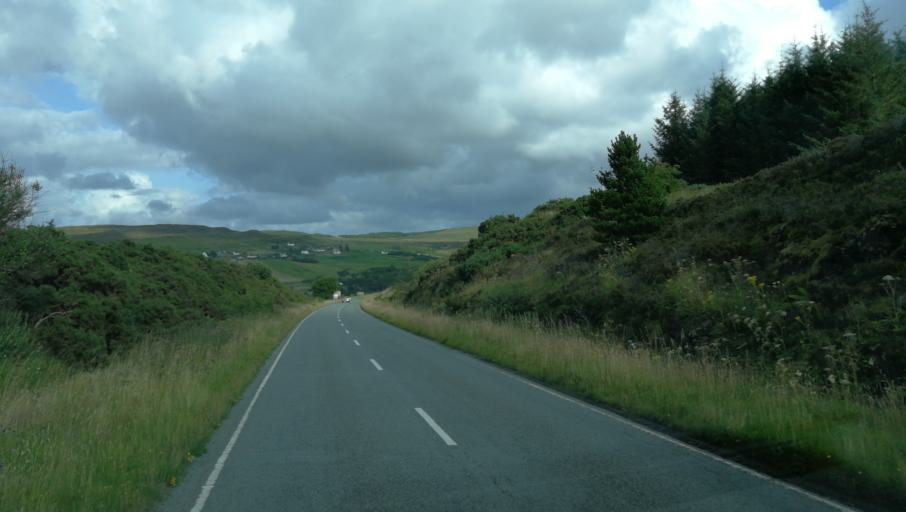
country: GB
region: Scotland
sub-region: Highland
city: Isle of Skye
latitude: 57.4723
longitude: -6.4451
